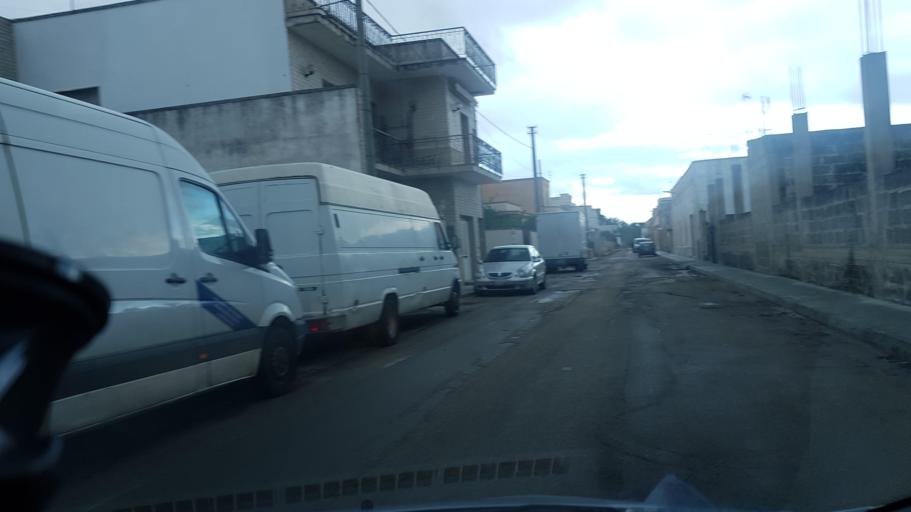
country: IT
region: Apulia
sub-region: Provincia di Lecce
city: Novoli
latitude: 40.3674
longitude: 18.0695
